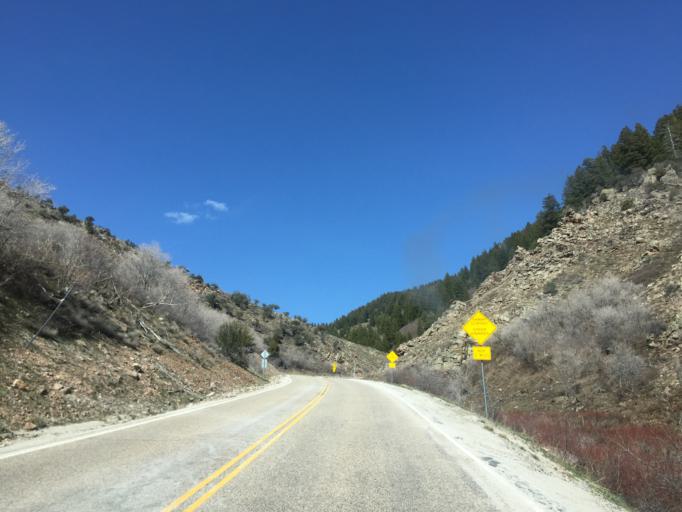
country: US
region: Utah
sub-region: Weber County
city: Wolf Creek
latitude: 41.3591
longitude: -111.7880
